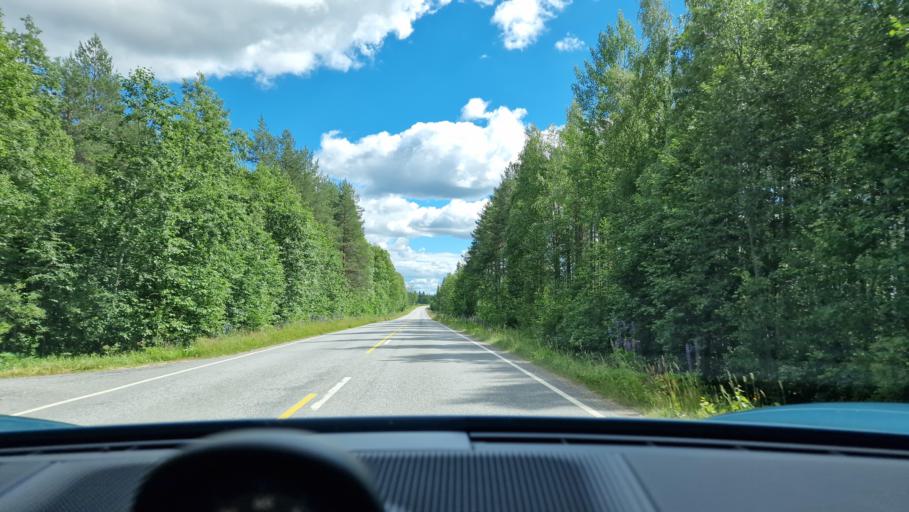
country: FI
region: Southern Ostrobothnia
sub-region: Jaerviseutu
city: Soini
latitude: 62.8346
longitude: 24.3327
